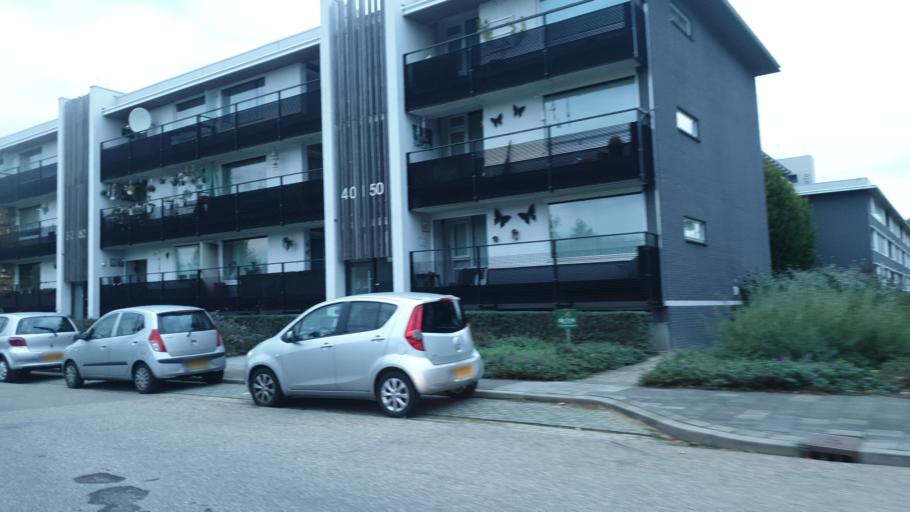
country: NL
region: Gelderland
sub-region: Gemeente Nijmegen
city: Lindenholt
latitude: 51.8322
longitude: 5.8111
